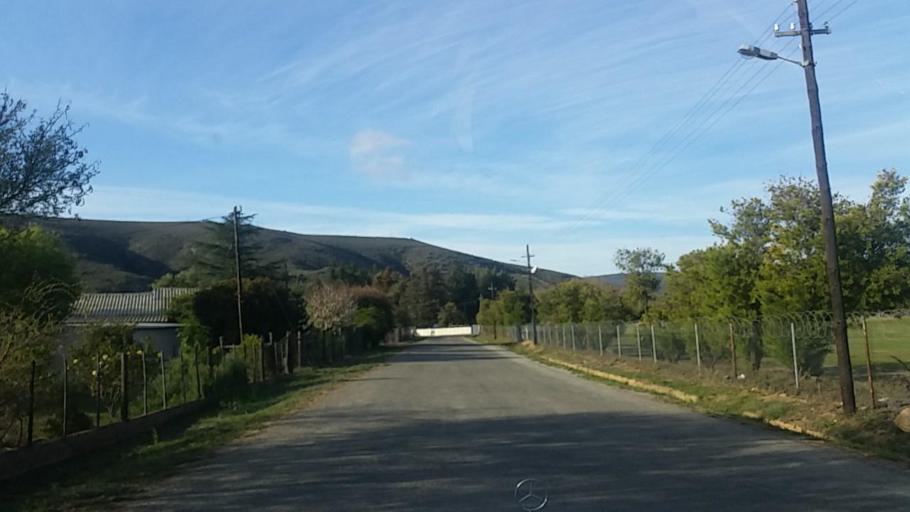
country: ZA
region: Western Cape
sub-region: Eden District Municipality
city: Knysna
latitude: -33.6574
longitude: 23.1217
